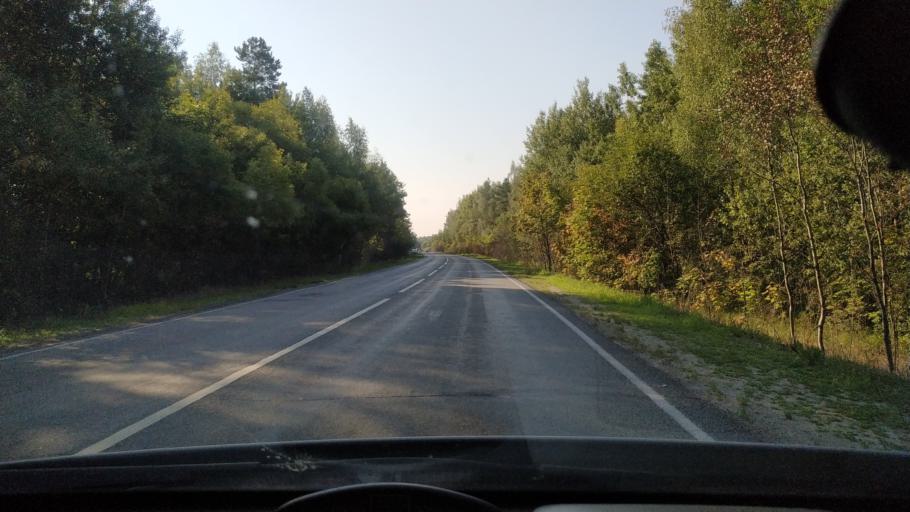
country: RU
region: Moskovskaya
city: Tugolesskiy Bor
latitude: 55.5381
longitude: 39.7059
